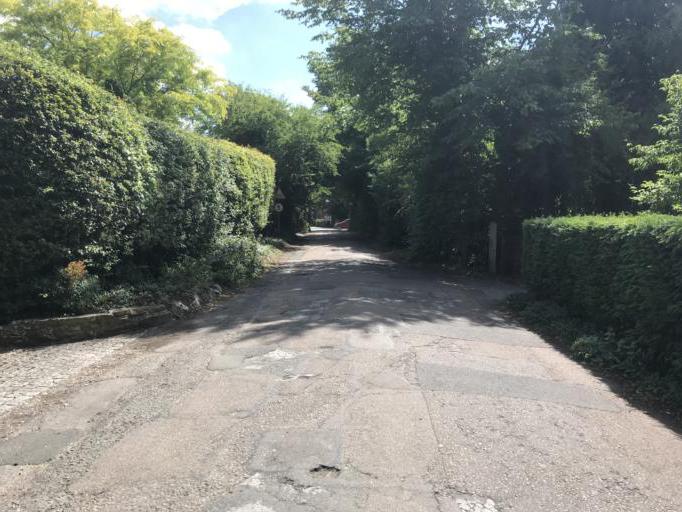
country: GB
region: England
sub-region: Cambridgeshire
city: Cambridge
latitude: 52.1900
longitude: 0.1212
